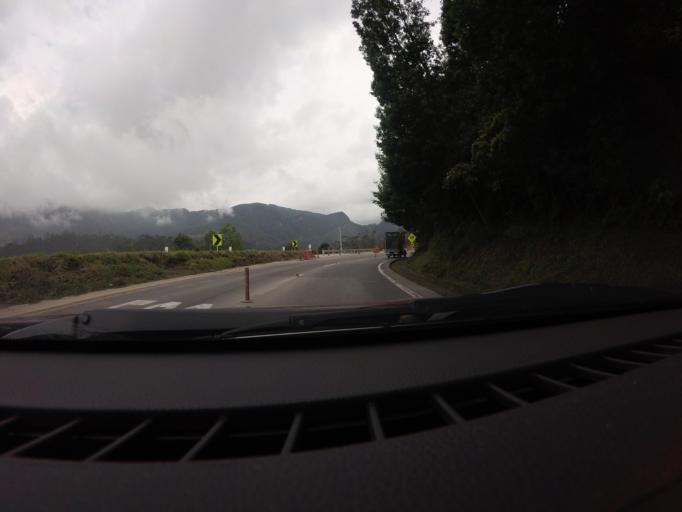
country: CO
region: Cundinamarca
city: San Francisco
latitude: 4.9194
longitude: -74.2927
